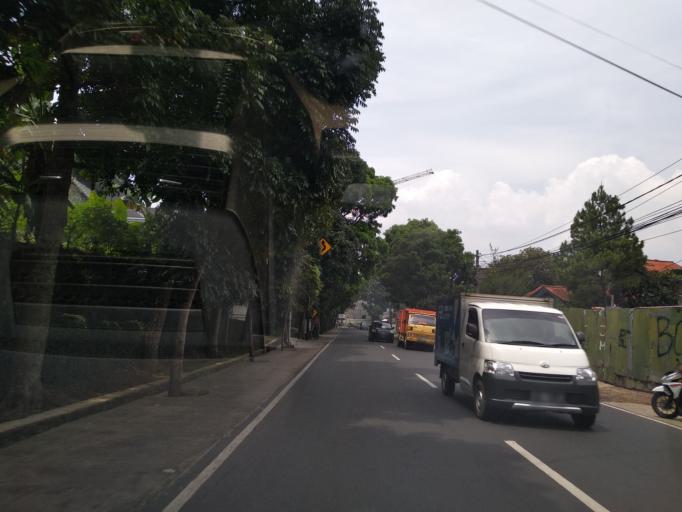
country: ID
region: West Java
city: Lembang
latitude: -6.8436
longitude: 107.5987
